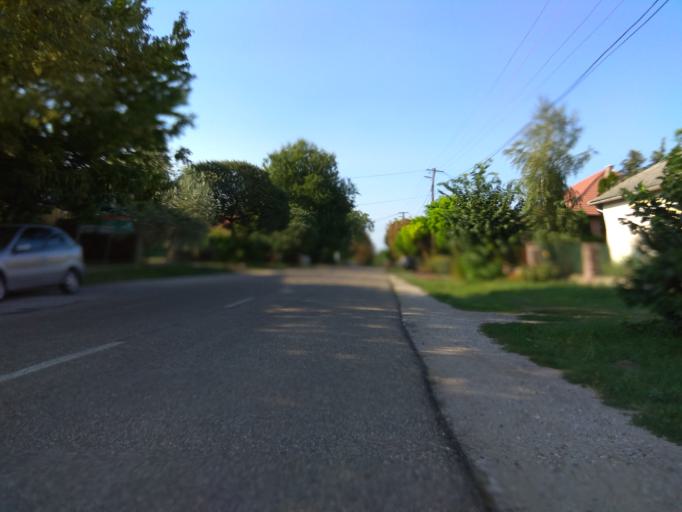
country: HU
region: Borsod-Abauj-Zemplen
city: Onod
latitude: 47.9630
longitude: 20.8839
